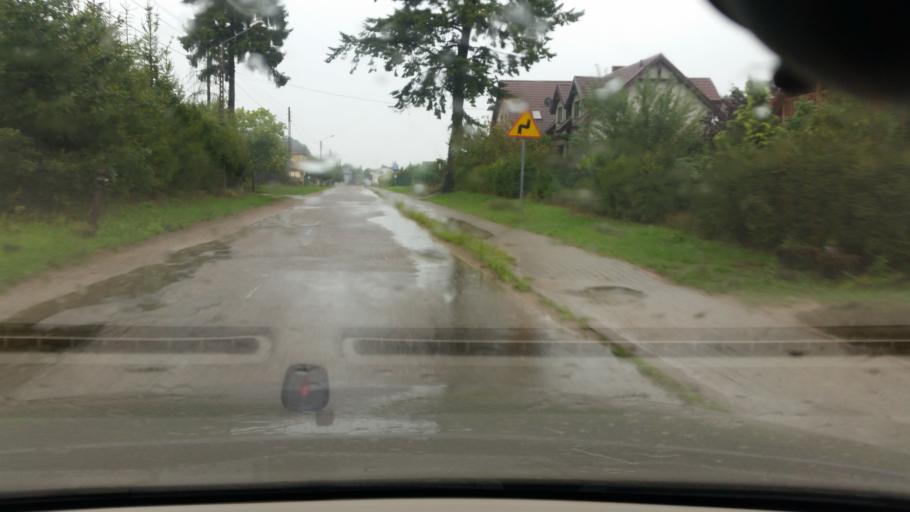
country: PL
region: Pomeranian Voivodeship
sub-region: Powiat wejherowski
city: Choczewo
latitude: 54.7684
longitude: 17.7937
